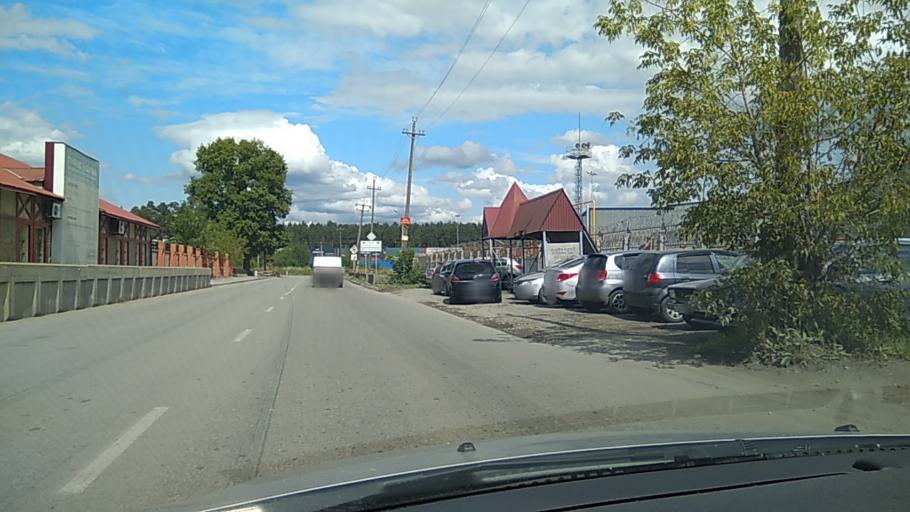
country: RU
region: Sverdlovsk
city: Shuvakish
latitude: 56.8867
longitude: 60.5359
